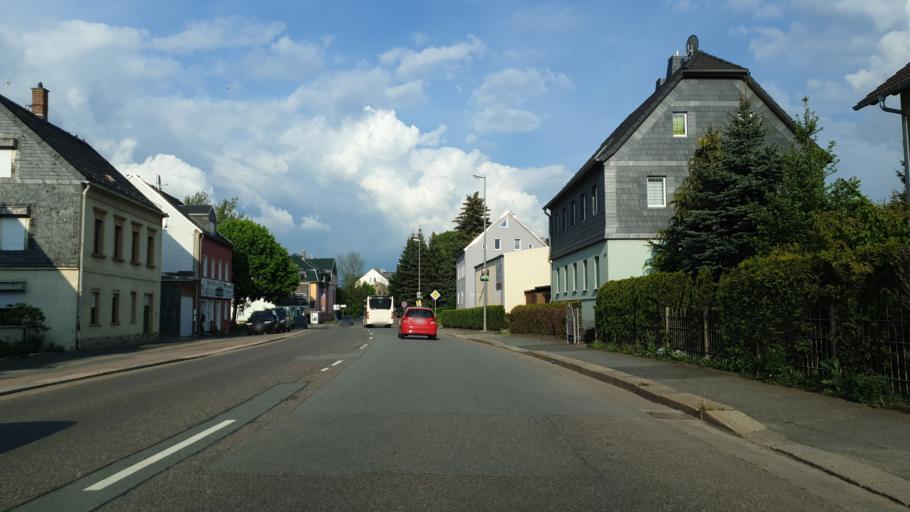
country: DE
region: Saxony
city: Neukirchen
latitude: 50.8194
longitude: 12.8615
